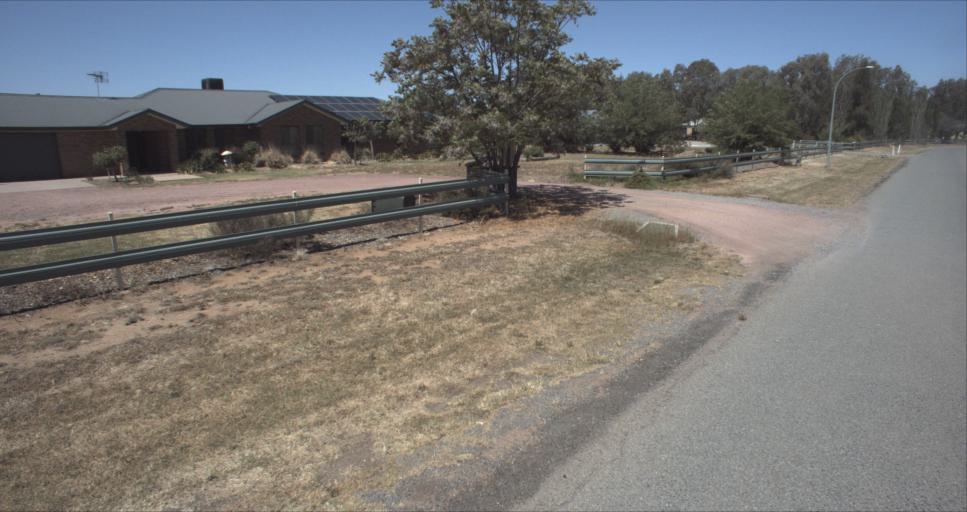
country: AU
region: New South Wales
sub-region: Leeton
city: Leeton
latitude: -34.5285
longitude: 146.3987
